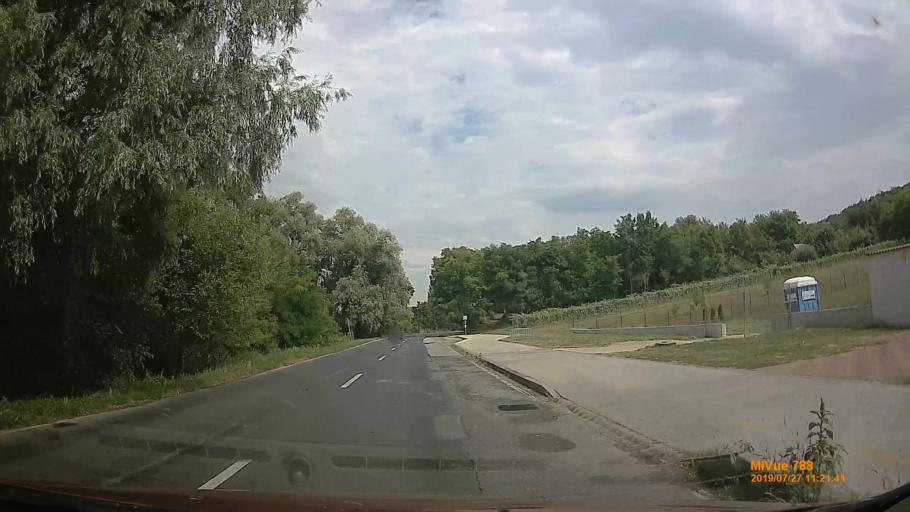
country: HU
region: Veszprem
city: Ajka
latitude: 47.1220
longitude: 17.5658
